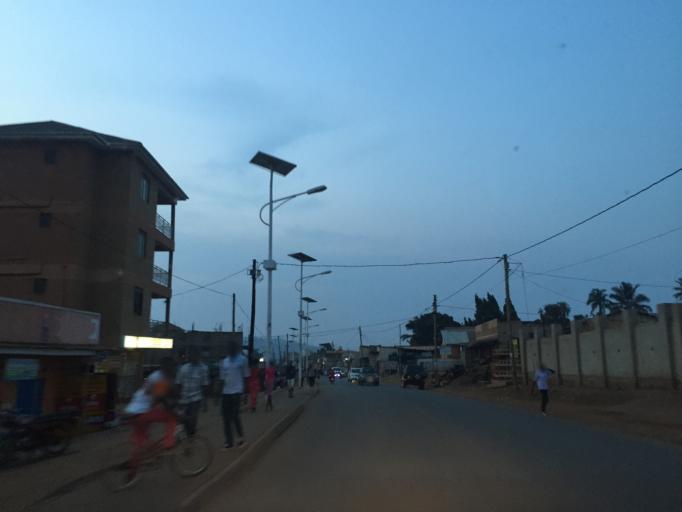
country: UG
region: Central Region
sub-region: Kampala District
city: Kampala
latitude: 0.3039
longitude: 32.6016
